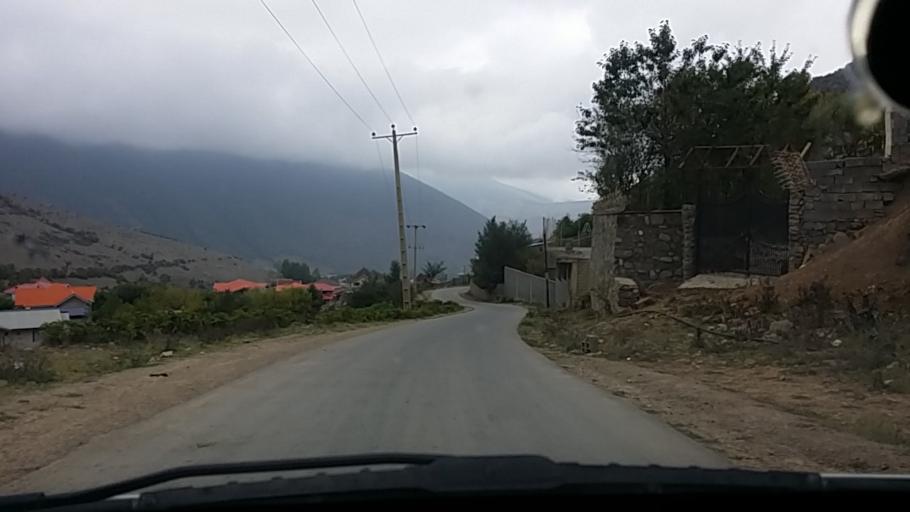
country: IR
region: Mazandaran
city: `Abbasabad
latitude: 36.4719
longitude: 51.1402
